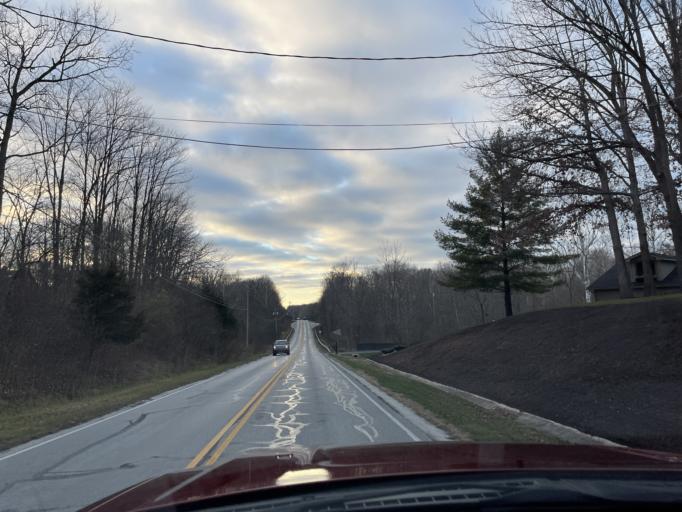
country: US
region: Indiana
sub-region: Hendricks County
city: Avon
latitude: 39.7771
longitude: -86.4119
